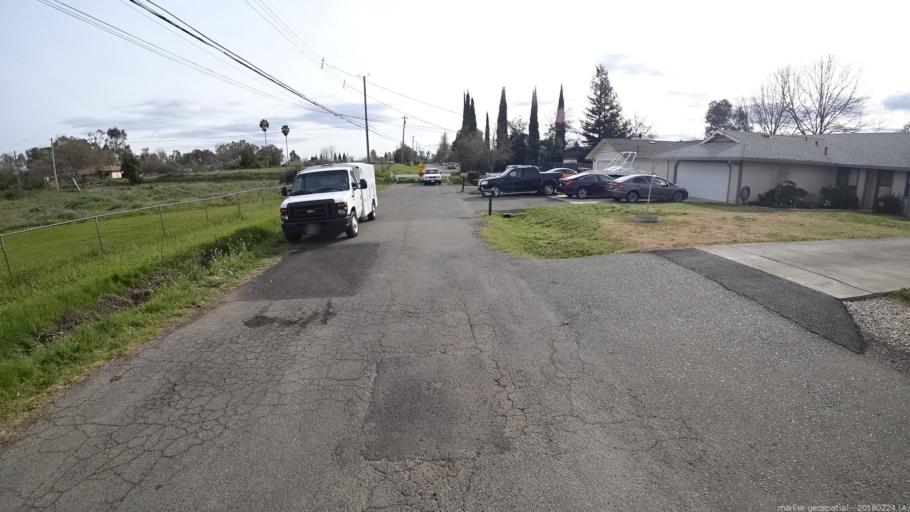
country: US
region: California
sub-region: Sacramento County
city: Elverta
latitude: 38.7082
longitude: -121.4570
